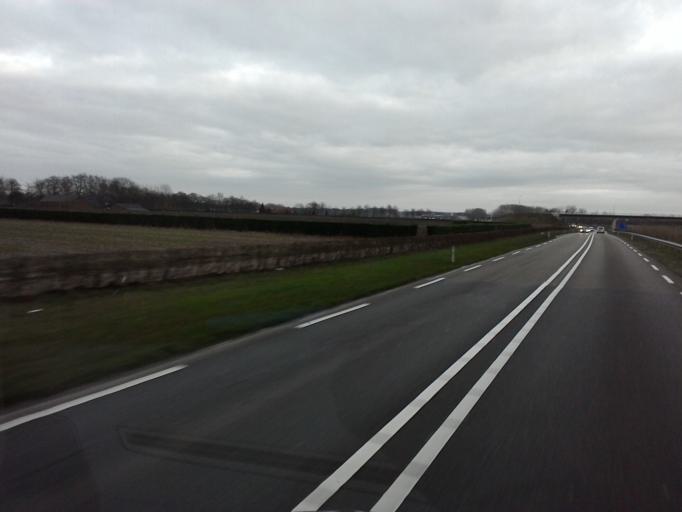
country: NL
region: North Brabant
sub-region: Gemeente Schijndel
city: Schijndel
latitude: 51.6600
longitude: 5.4071
